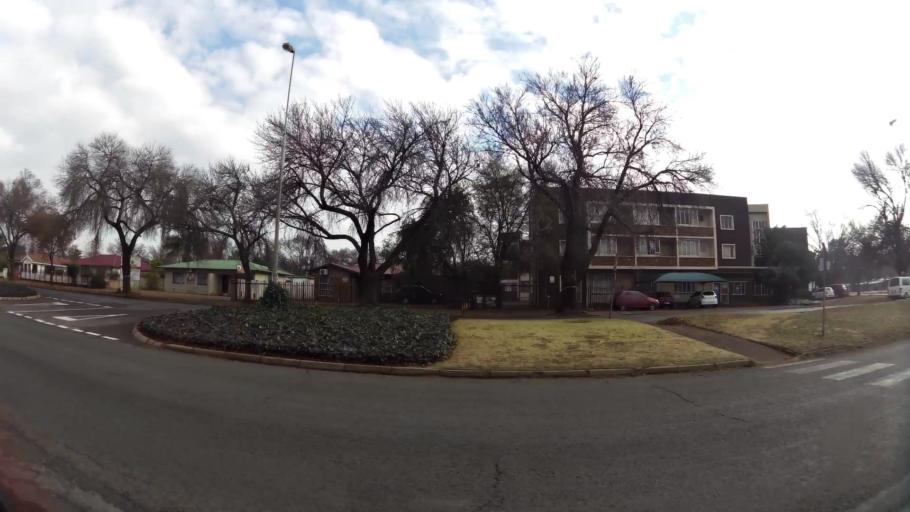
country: ZA
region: Gauteng
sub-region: Sedibeng District Municipality
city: Vanderbijlpark
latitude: -26.7033
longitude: 27.8313
